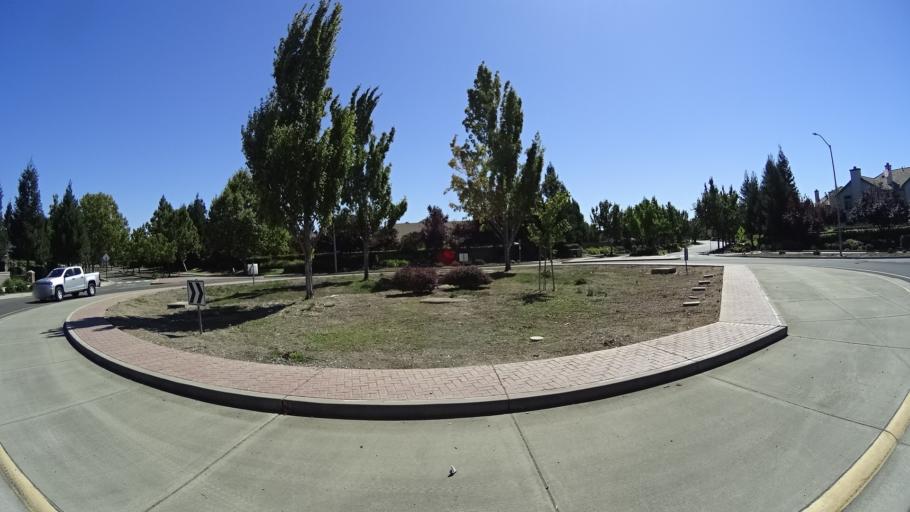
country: US
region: California
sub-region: Sacramento County
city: Elk Grove
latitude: 38.4093
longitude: -121.3391
